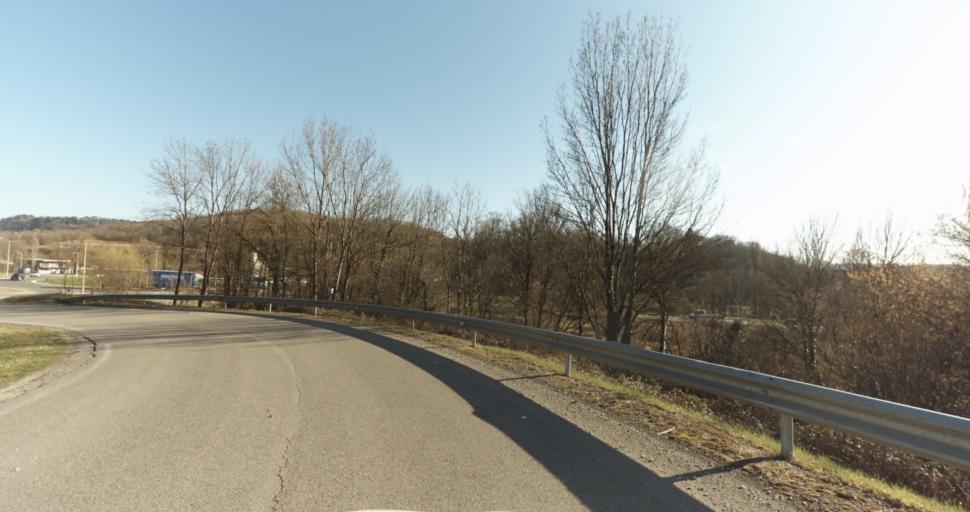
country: FR
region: Franche-Comte
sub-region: Departement du Jura
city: Montmorot
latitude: 46.6784
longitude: 5.5087
